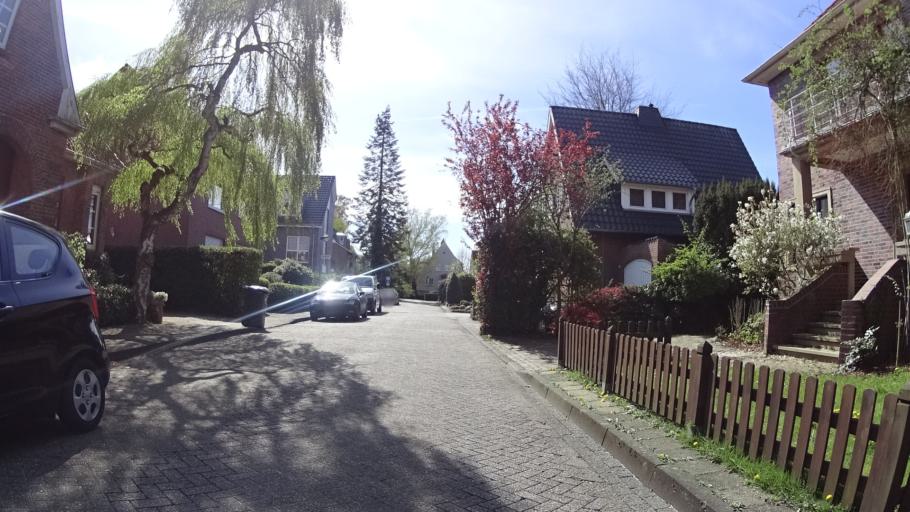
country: DE
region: Lower Saxony
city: Lingen
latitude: 52.5186
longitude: 7.3136
